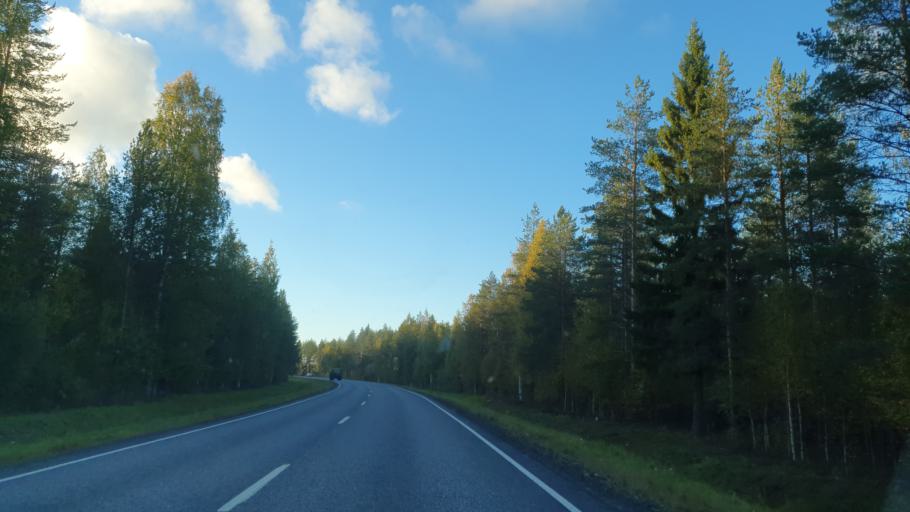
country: FI
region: Kainuu
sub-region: Kehys-Kainuu
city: Kuhmo
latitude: 64.0603
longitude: 29.5356
